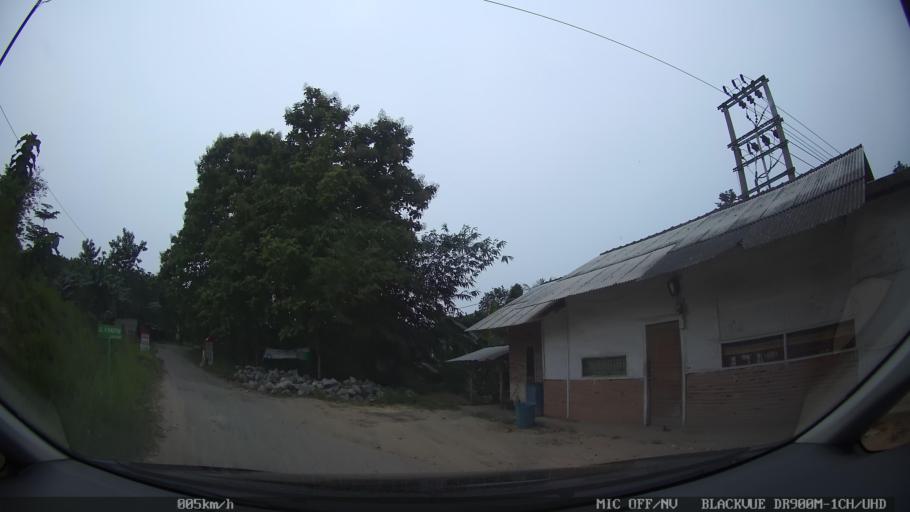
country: ID
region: Lampung
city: Panjang
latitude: -5.4023
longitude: 105.3560
